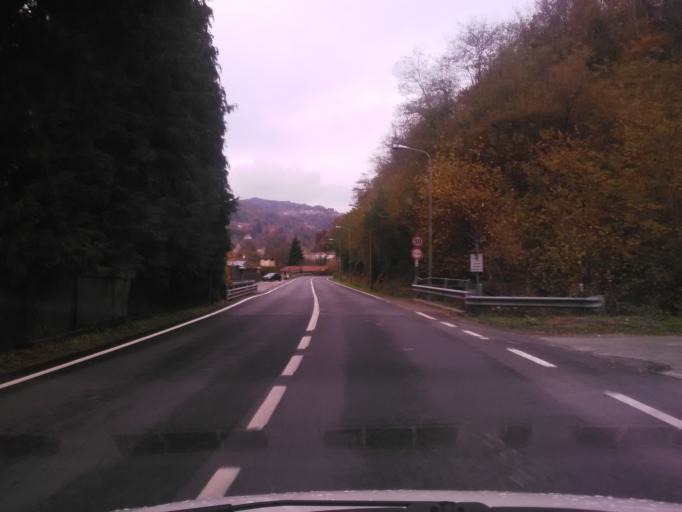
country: IT
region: Piedmont
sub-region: Provincia di Vercelli
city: Valduggia
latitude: 45.7242
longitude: 8.3273
